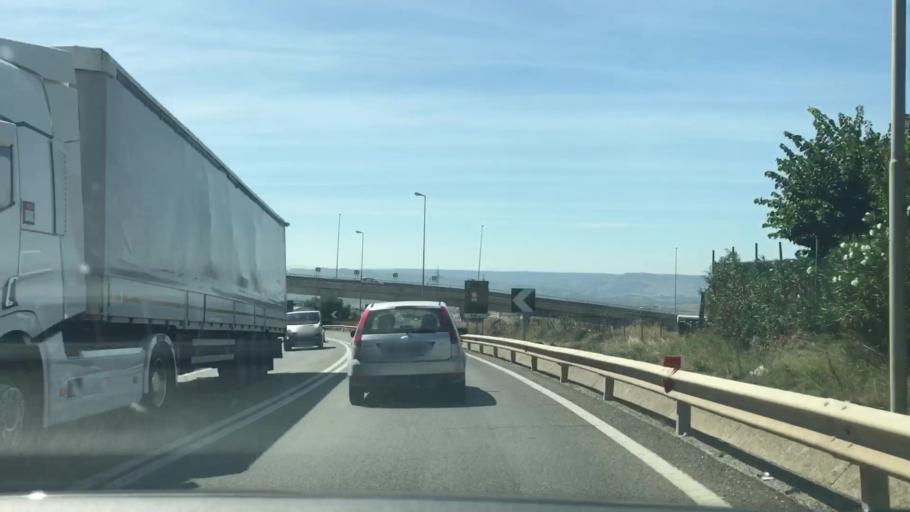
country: IT
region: Basilicate
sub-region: Provincia di Matera
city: Matera
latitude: 40.6740
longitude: 16.5777
